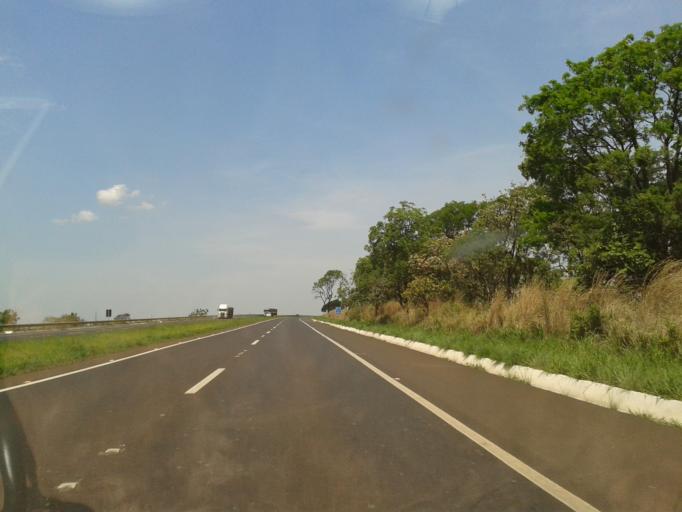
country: BR
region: Minas Gerais
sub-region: Monte Alegre De Minas
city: Monte Alegre de Minas
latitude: -18.8523
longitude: -48.7852
